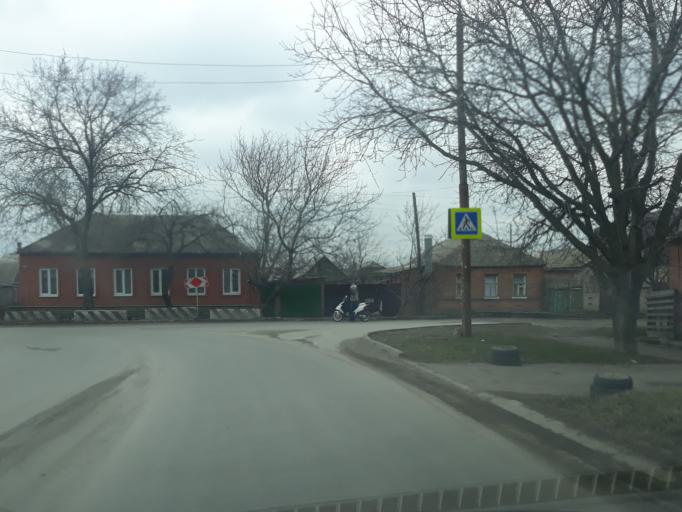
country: RU
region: Rostov
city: Taganrog
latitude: 47.2669
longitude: 38.8916
